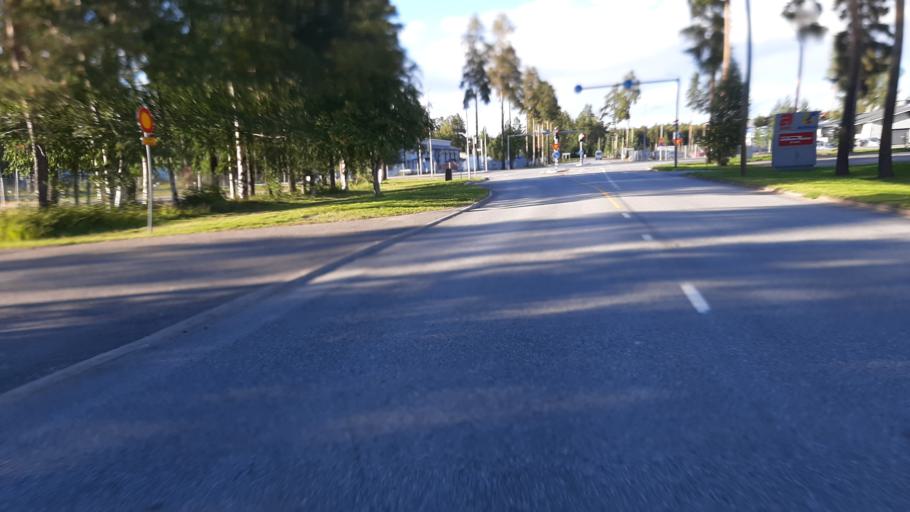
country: FI
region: North Karelia
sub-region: Joensuu
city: Joensuu
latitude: 62.6272
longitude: 29.7711
